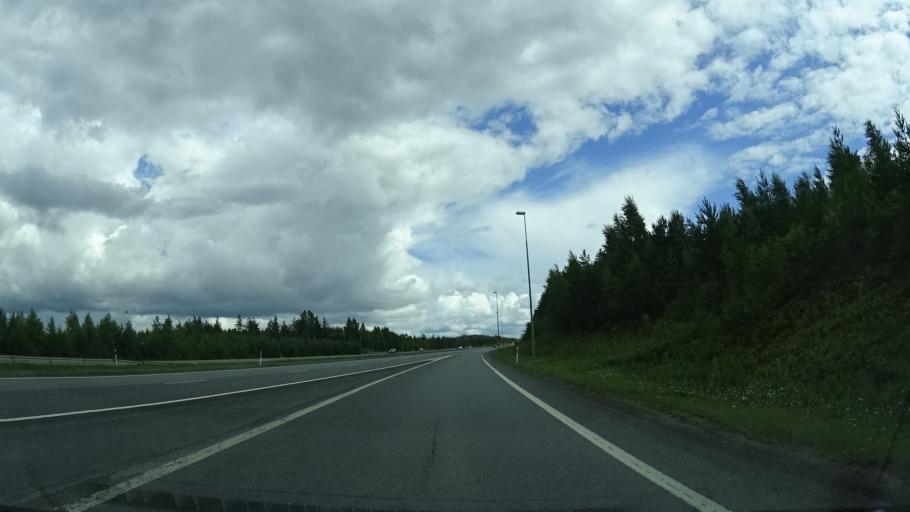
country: FI
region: Haeme
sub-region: Haemeenlinna
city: Kalvola
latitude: 61.1396
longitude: 24.0668
